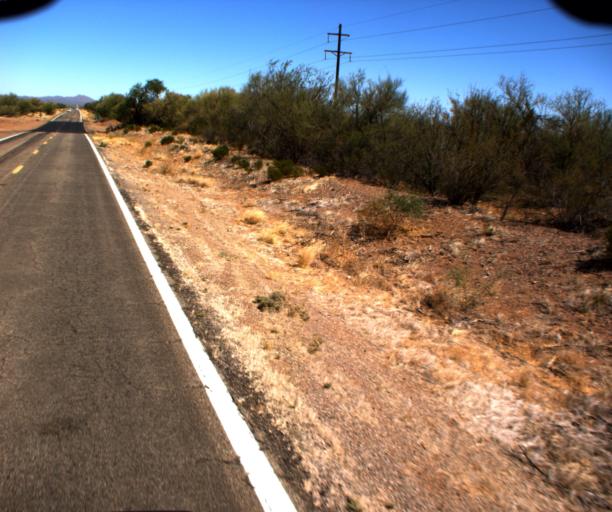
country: US
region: Arizona
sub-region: Pima County
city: Sells
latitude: 32.0527
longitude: -112.0274
